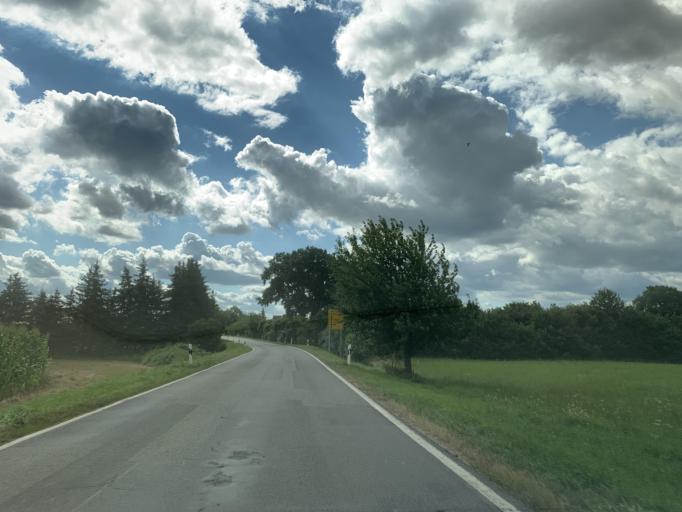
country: DE
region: Mecklenburg-Vorpommern
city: Blankensee
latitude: 53.4137
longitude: 13.2239
